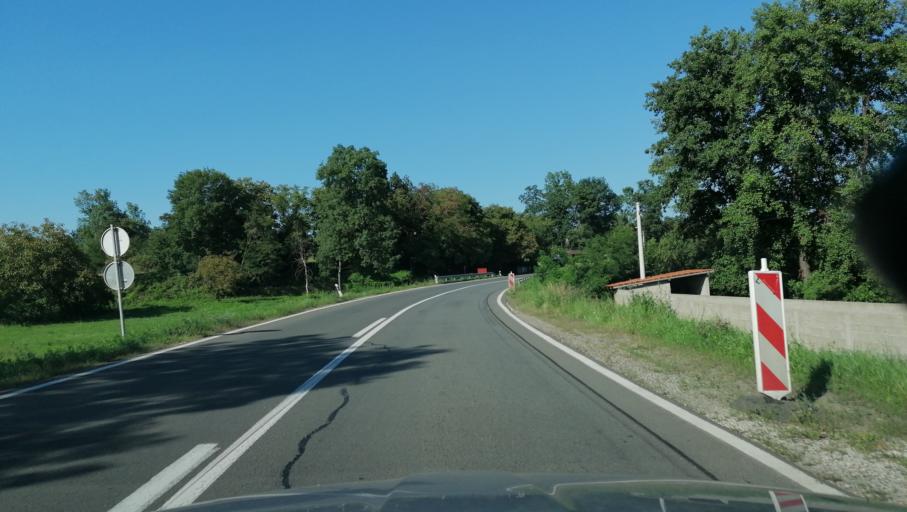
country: RS
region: Central Serbia
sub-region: Raski Okrug
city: Kraljevo
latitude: 43.6931
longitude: 20.5816
